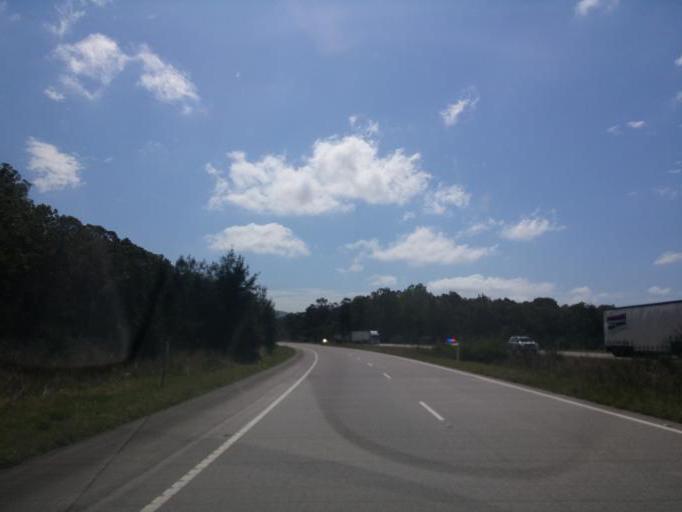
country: AU
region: New South Wales
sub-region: Great Lakes
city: Hawks Nest
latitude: -32.5559
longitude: 152.1486
